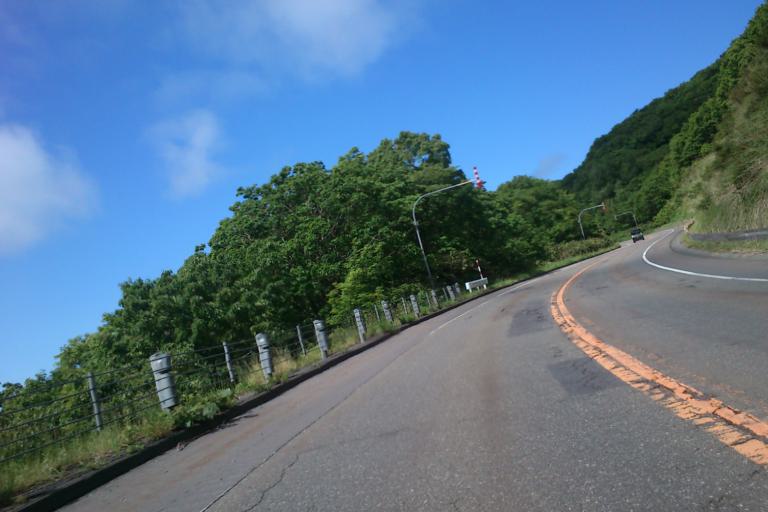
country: JP
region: Hokkaido
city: Ishikari
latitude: 43.4818
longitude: 141.3966
